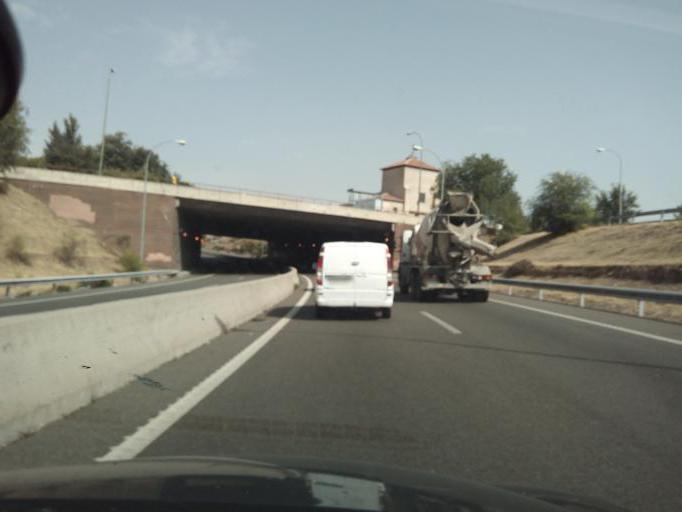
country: ES
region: Madrid
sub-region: Provincia de Madrid
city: Barajas de Madrid
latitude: 40.4667
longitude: -3.5813
